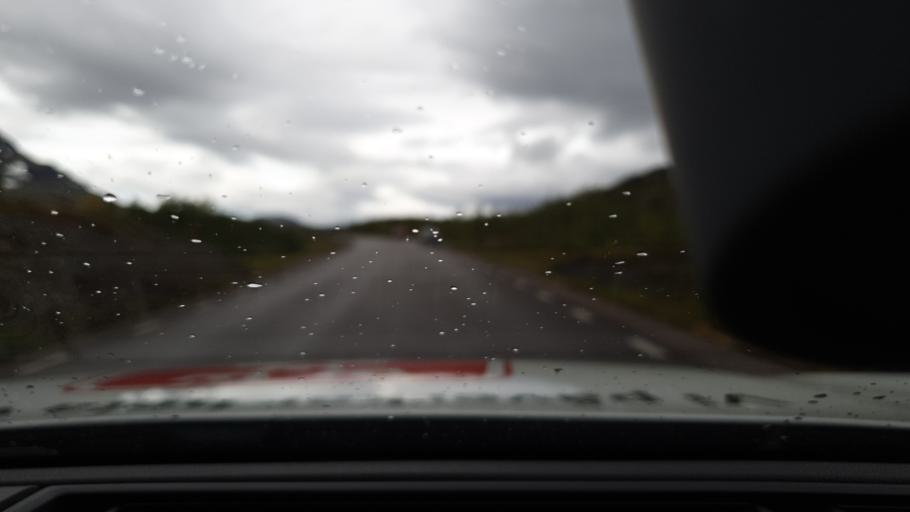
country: NO
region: Troms
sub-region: Bardu
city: Setermoen
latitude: 68.4275
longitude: 18.3293
